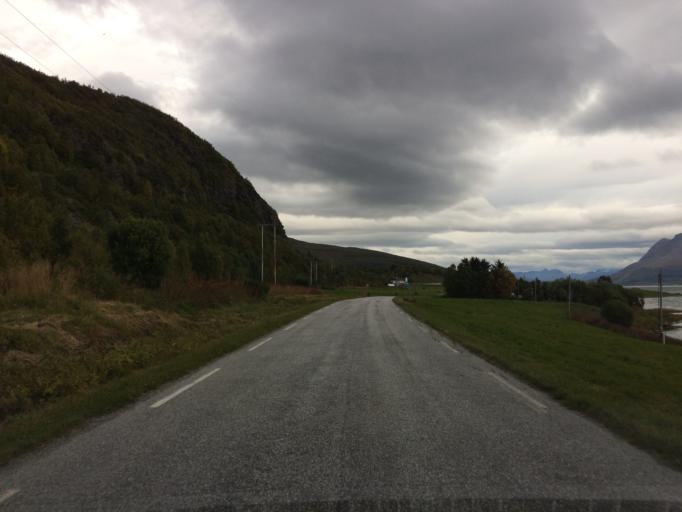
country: NO
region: Troms
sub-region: Sorreisa
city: Sorreisa
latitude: 69.5242
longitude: 18.2439
